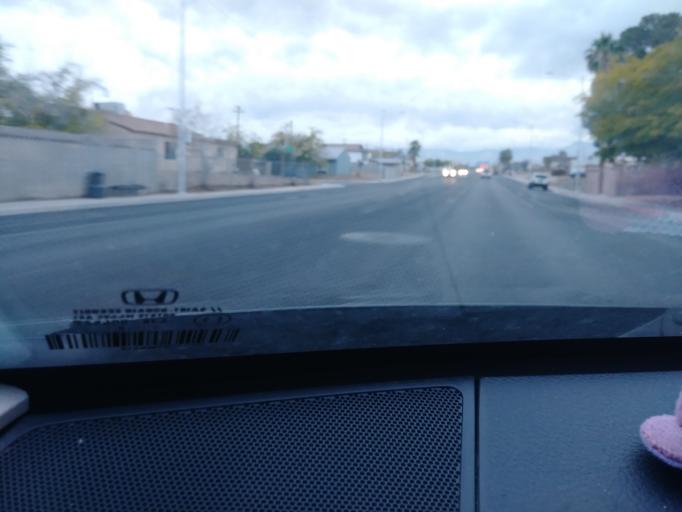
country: US
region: Nevada
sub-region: Clark County
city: Spring Valley
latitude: 36.1664
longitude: -115.2264
